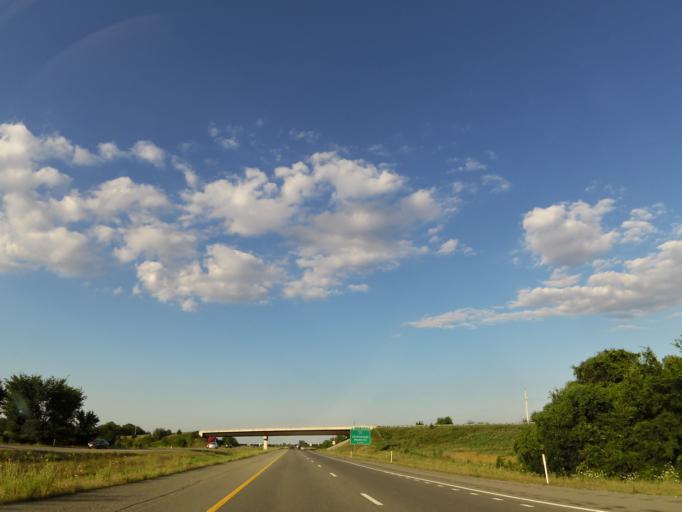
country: US
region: Tennessee
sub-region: Rutherford County
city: Smyrna
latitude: 35.8704
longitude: -86.5031
